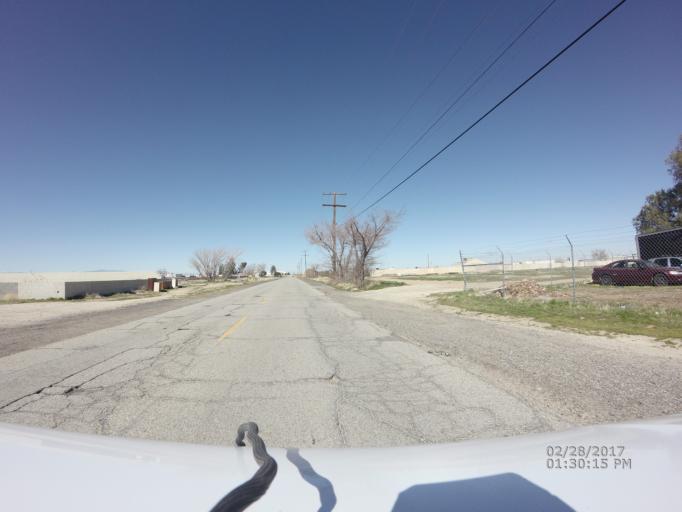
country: US
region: California
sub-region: Los Angeles County
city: Palmdale
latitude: 34.5920
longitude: -118.1164
